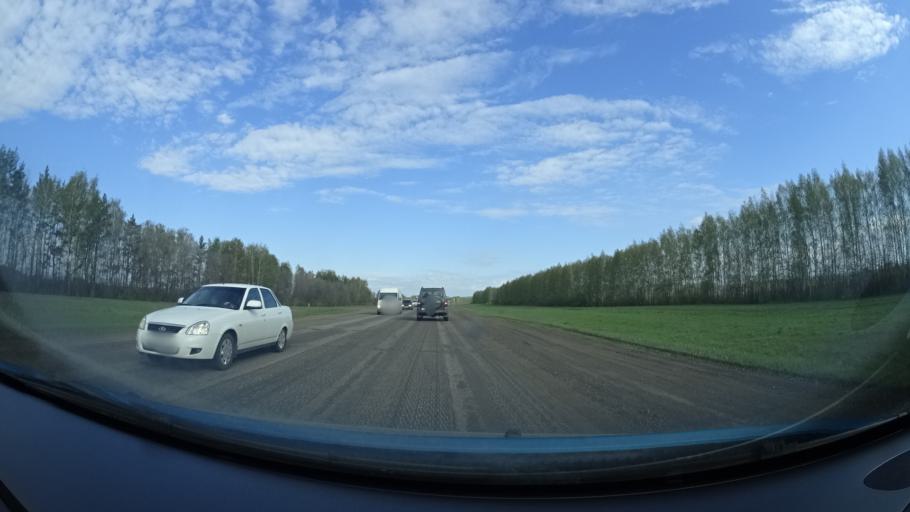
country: RU
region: Bashkortostan
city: Blagoveshchensk
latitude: 55.2374
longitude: 55.7741
